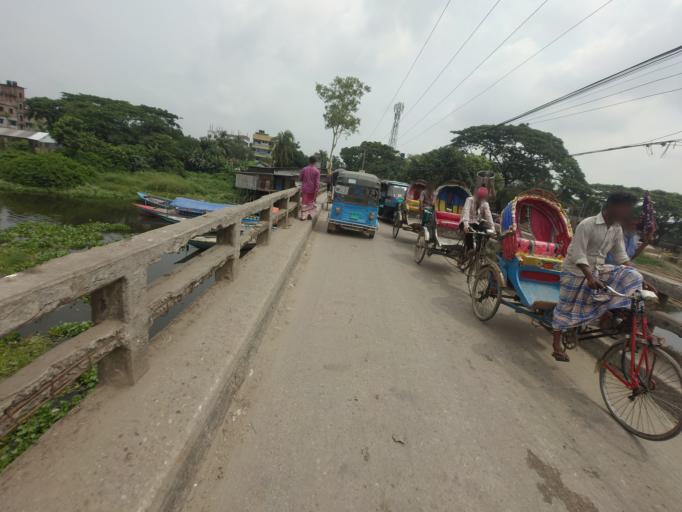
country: BD
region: Dhaka
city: Azimpur
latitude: 23.7308
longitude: 90.3341
